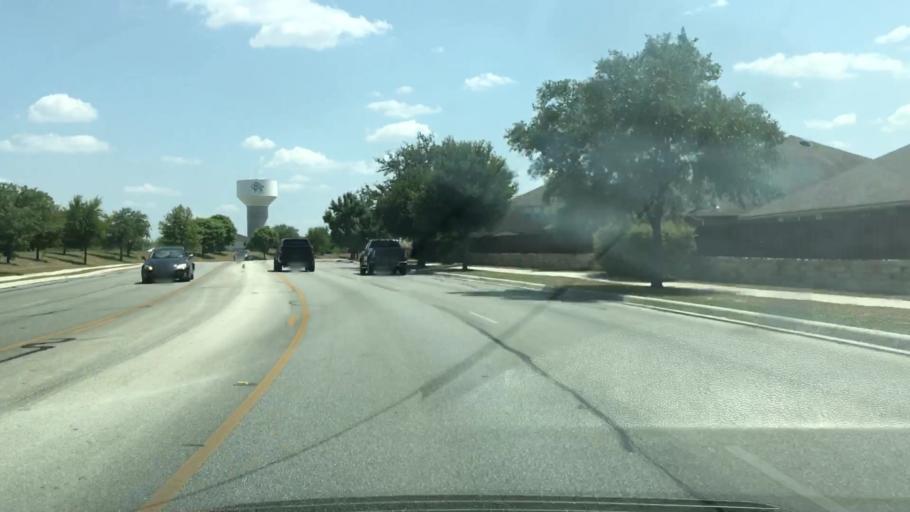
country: US
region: Texas
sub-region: Guadalupe County
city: Cibolo
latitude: 29.5888
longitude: -98.2493
